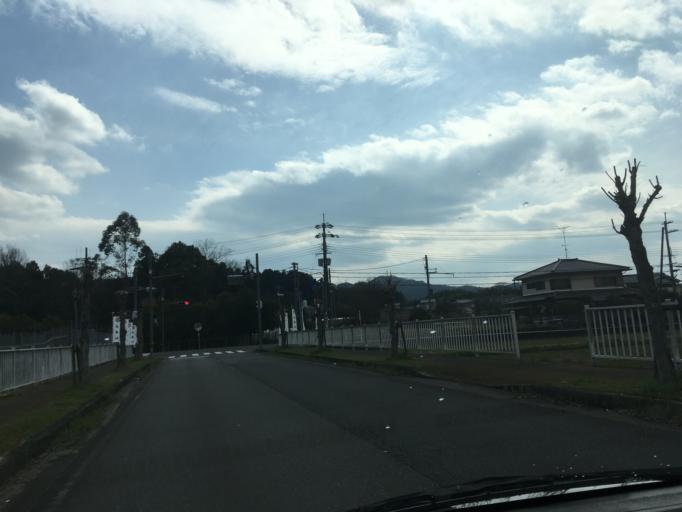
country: JP
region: Nara
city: Gose
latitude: 34.4491
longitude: 135.7914
